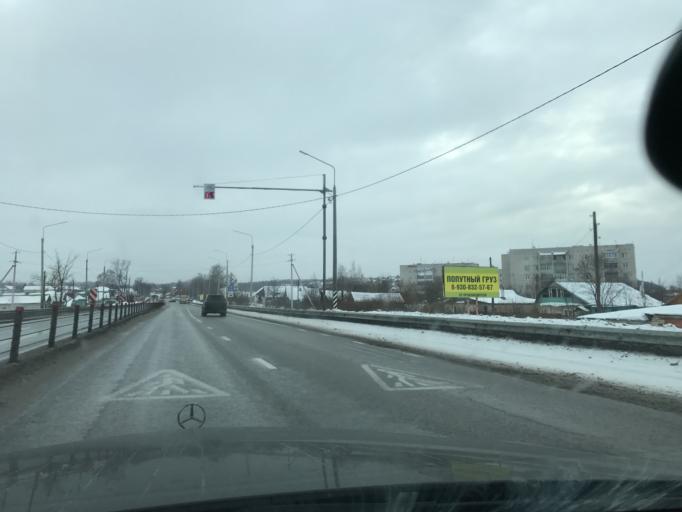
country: RU
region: Vladimir
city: Gorokhovets
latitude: 56.1994
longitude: 42.7074
